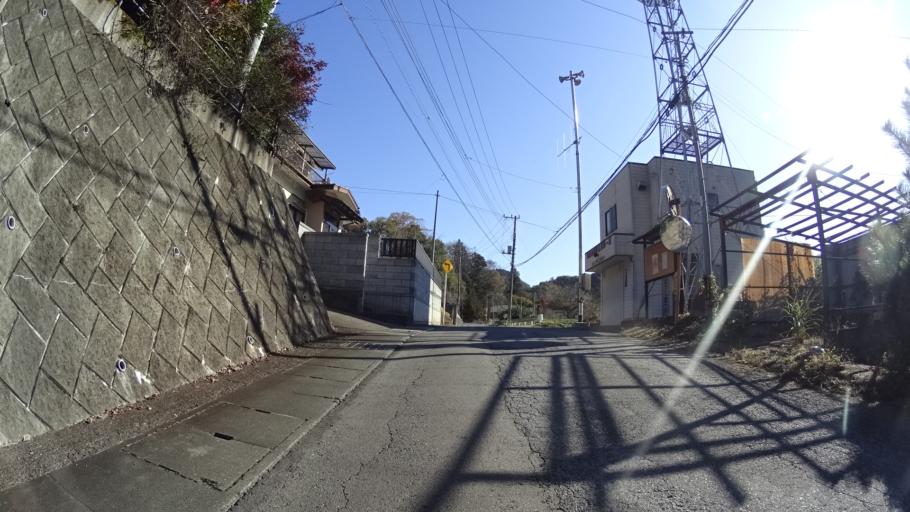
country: JP
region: Yamanashi
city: Uenohara
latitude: 35.6726
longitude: 139.0913
